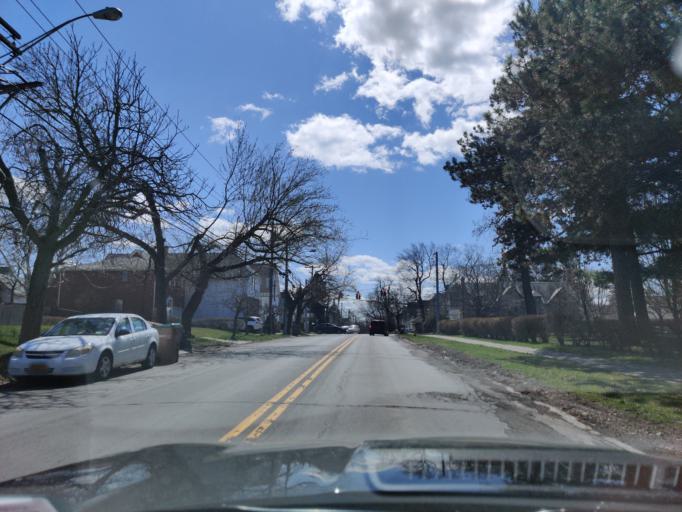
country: US
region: New York
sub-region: Erie County
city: Sloan
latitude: 42.9103
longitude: -78.7964
